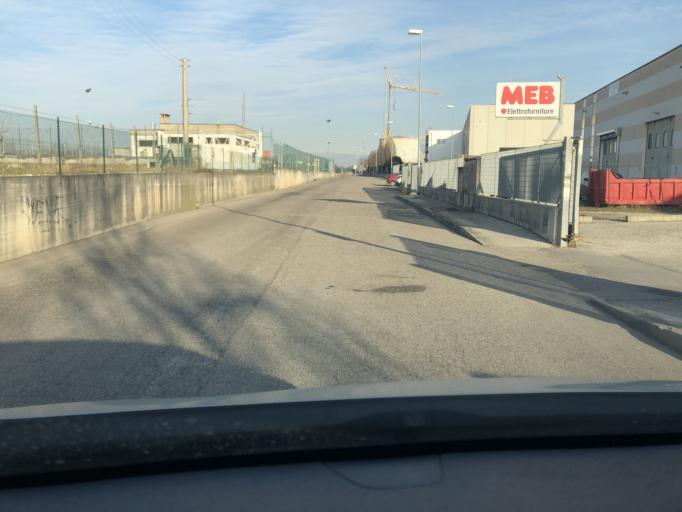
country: IT
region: Veneto
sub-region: Provincia di Verona
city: Sona
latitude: 45.4361
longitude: 10.8564
